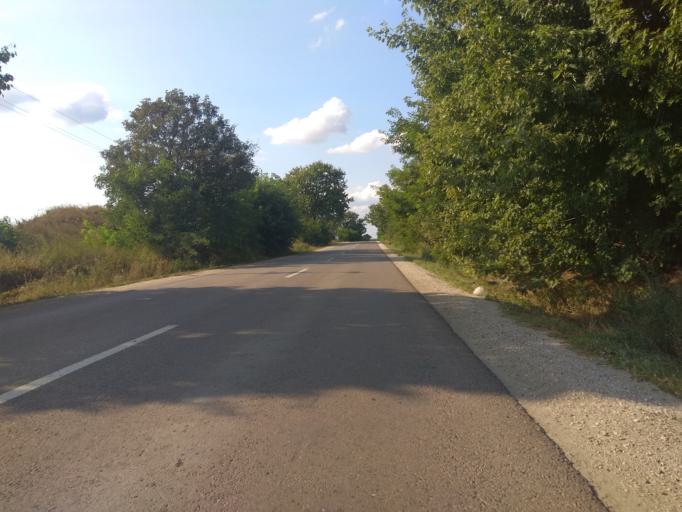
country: HU
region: Borsod-Abauj-Zemplen
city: Hejobaba
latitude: 47.8971
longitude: 20.8920
